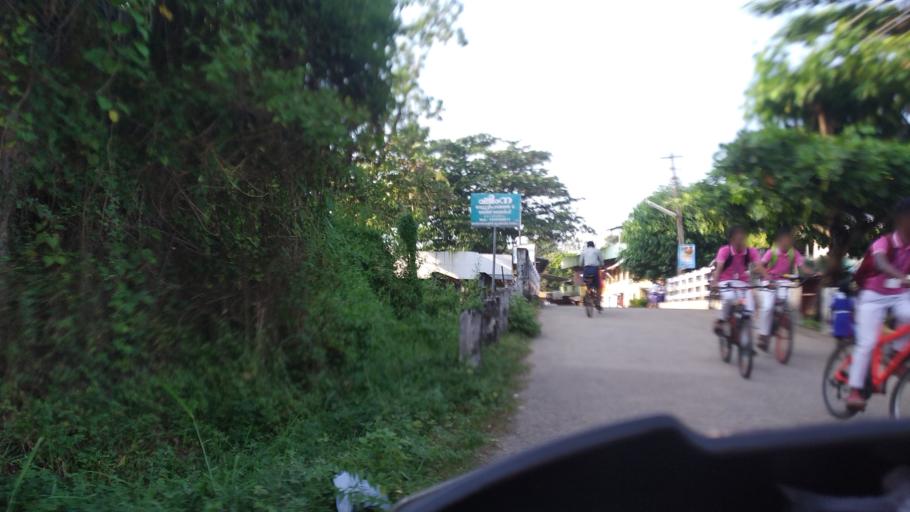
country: IN
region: Kerala
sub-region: Ernakulam
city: Elur
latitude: 10.0483
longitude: 76.2197
